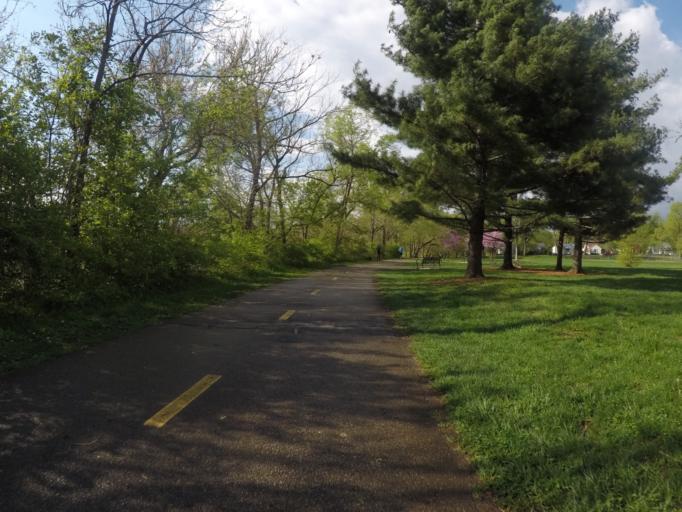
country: US
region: Ohio
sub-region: Franklin County
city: Grandview Heights
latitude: 40.0276
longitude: -83.0238
